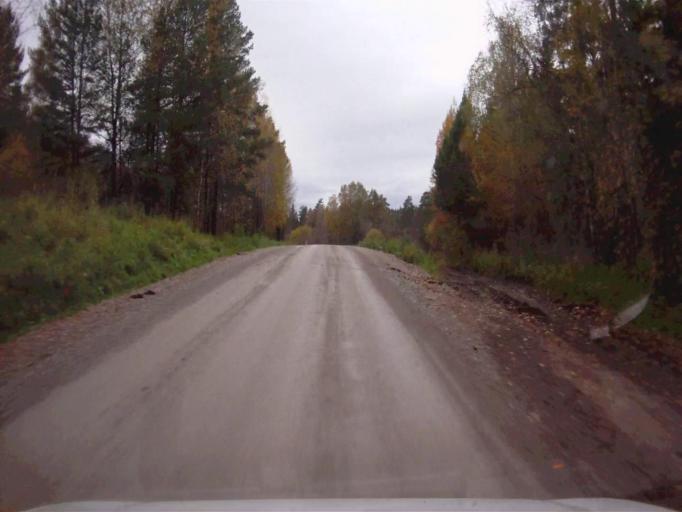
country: RU
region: Chelyabinsk
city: Nyazepetrovsk
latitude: 56.0493
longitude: 59.4979
